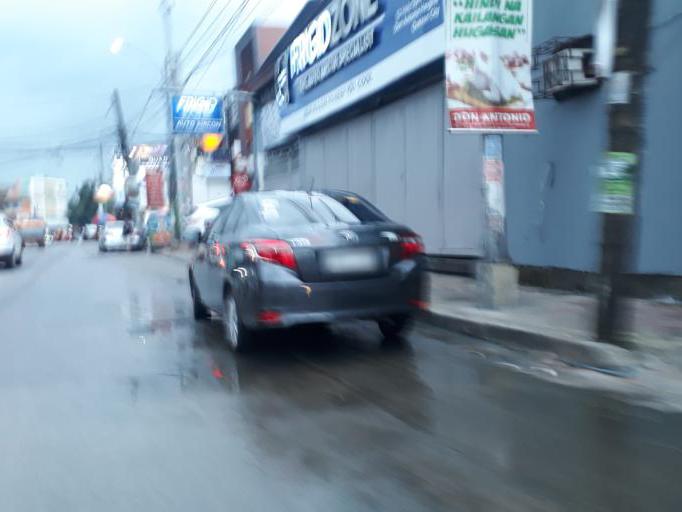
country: PH
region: Metro Manila
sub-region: Quezon City
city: Quezon City
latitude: 14.6817
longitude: 121.0802
